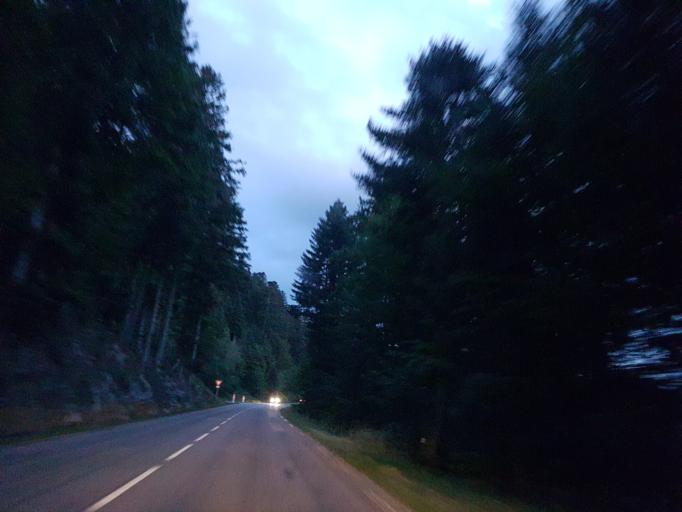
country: FR
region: Lorraine
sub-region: Departement des Vosges
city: Xonrupt-Longemer
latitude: 48.0790
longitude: 6.9501
